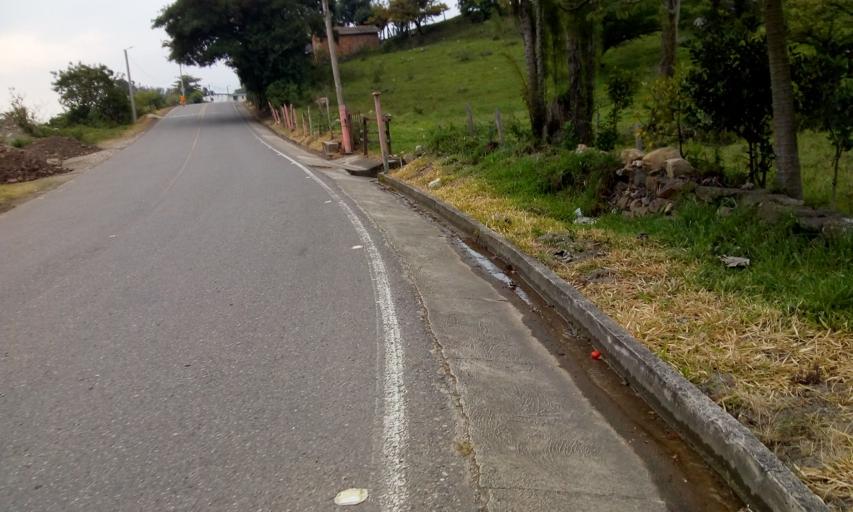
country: CO
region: Boyaca
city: Tipacoque
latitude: 6.4152
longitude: -72.6913
